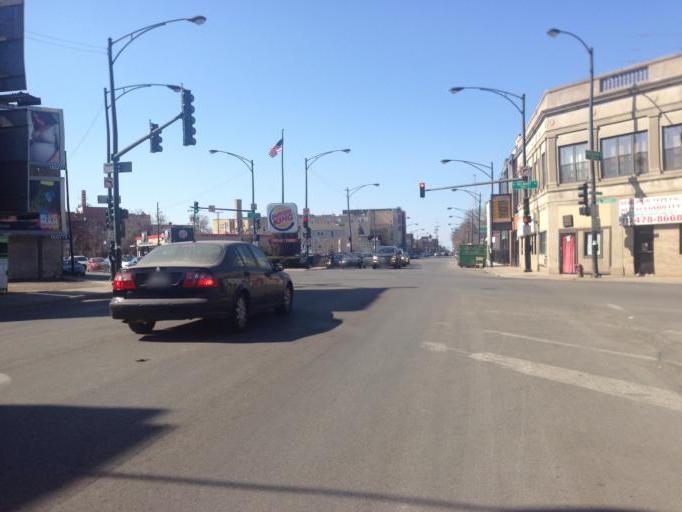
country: US
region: Illinois
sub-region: Cook County
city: Lincolnwood
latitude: 41.9392
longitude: -87.6980
